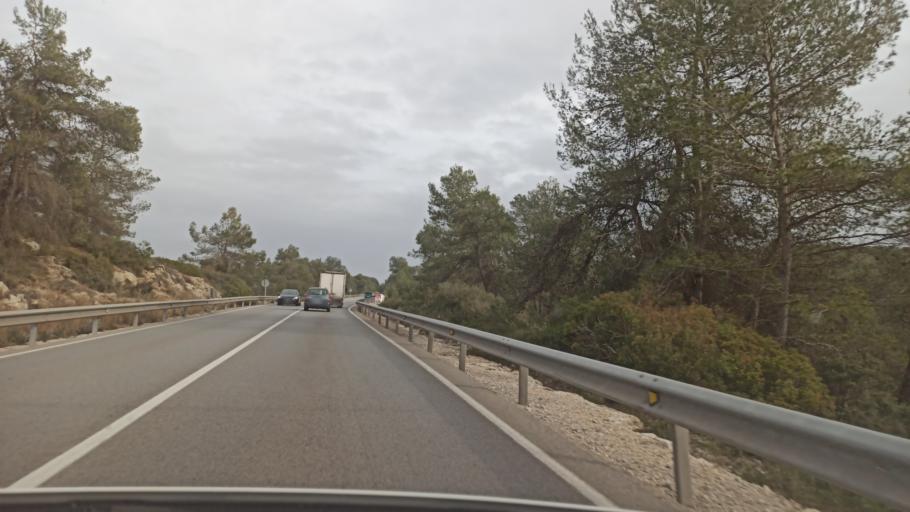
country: ES
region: Catalonia
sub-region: Provincia de Barcelona
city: Subirats
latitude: 41.3915
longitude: 1.8686
